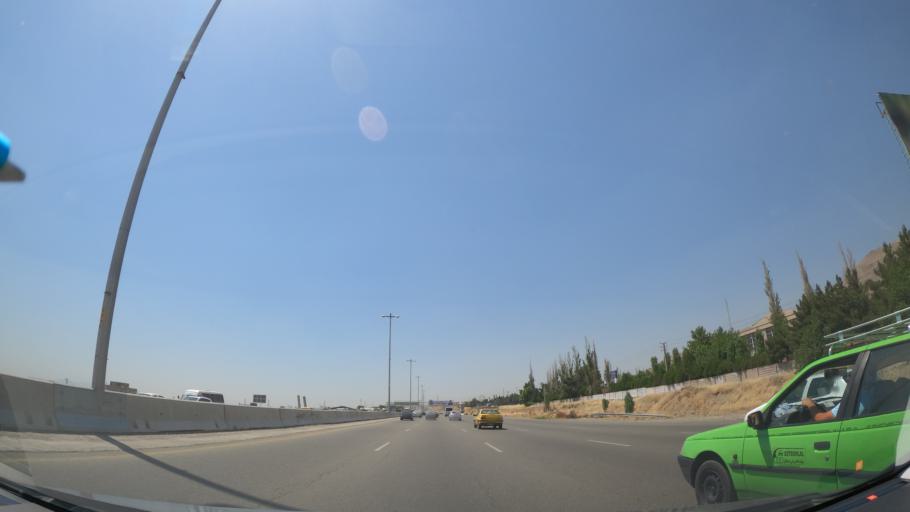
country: IR
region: Tehran
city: Shahr-e Qods
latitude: 35.7621
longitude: 51.0618
